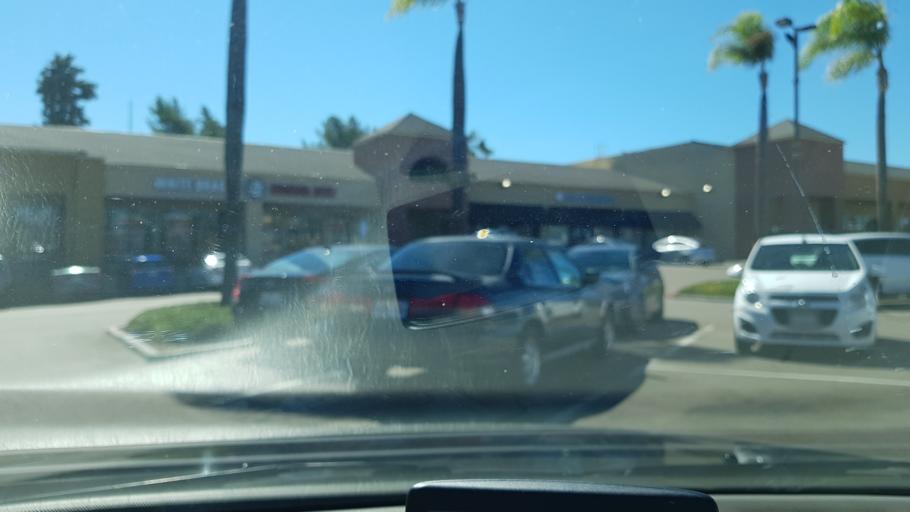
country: US
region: California
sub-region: San Diego County
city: Fairbanks Ranch
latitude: 32.9065
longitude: -117.1718
